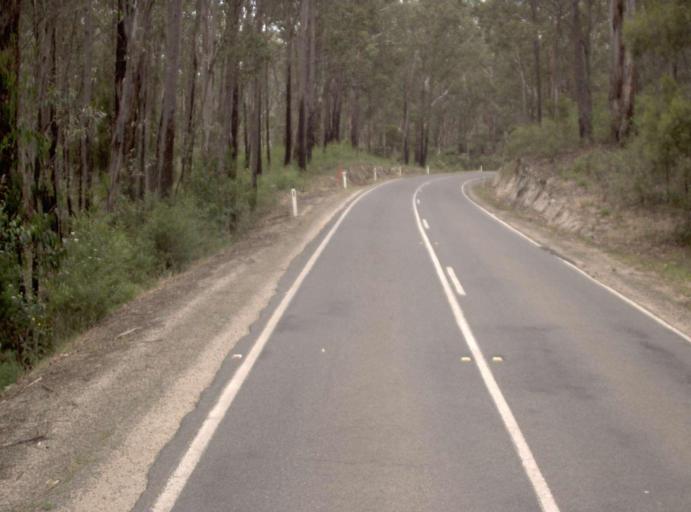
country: AU
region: Victoria
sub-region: Latrobe
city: Traralgon
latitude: -38.4268
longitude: 146.7436
